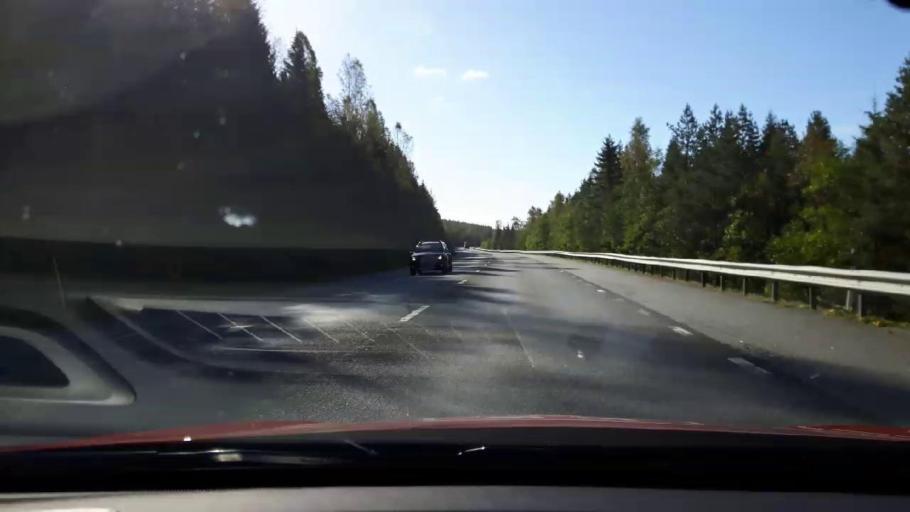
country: SE
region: Vaesternorrland
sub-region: Ange Kommun
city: Ange
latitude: 62.6582
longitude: 15.6177
